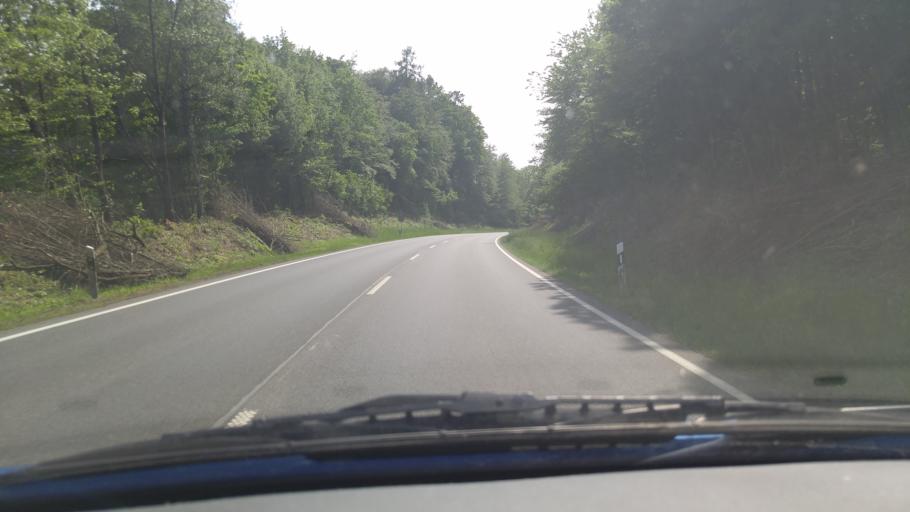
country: DE
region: Hesse
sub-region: Regierungsbezirk Giessen
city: Schotten
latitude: 50.4817
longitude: 9.0947
